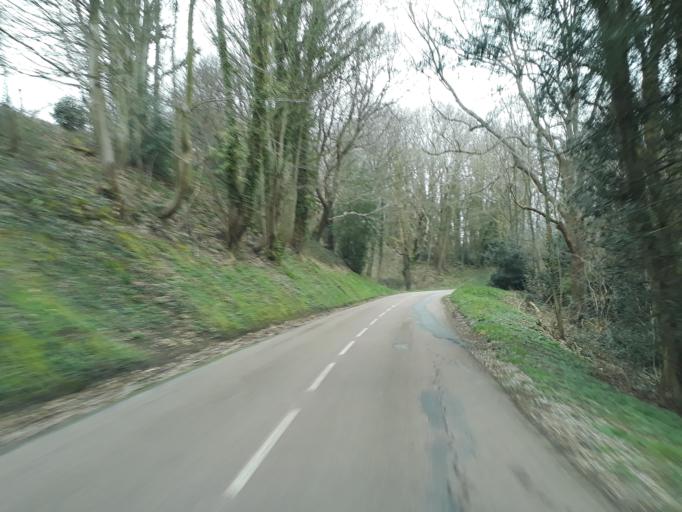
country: FR
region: Haute-Normandie
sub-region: Departement de la Seine-Maritime
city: Yport
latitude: 49.7304
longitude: 0.2896
